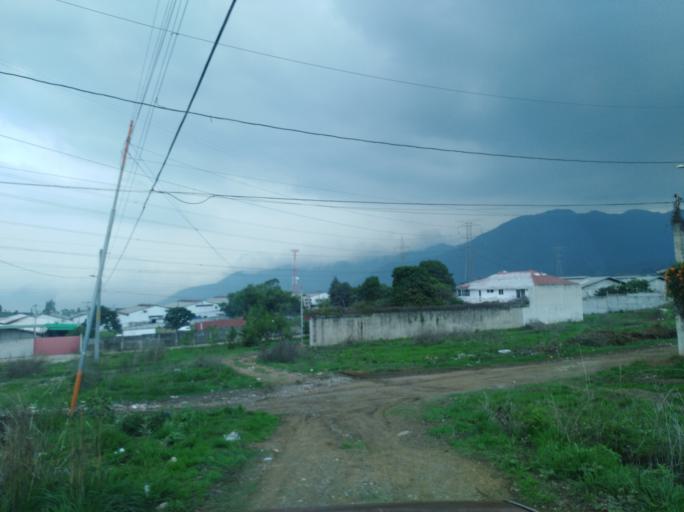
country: GT
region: Guatemala
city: Villa Nueva
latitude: 14.5228
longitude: -90.6224
